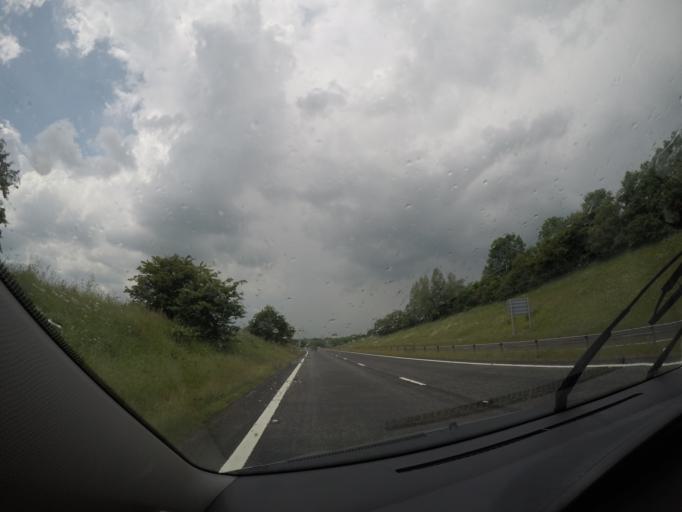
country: GB
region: England
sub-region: Cumbria
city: Appleby-in-Westmorland
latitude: 54.5855
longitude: -2.4910
